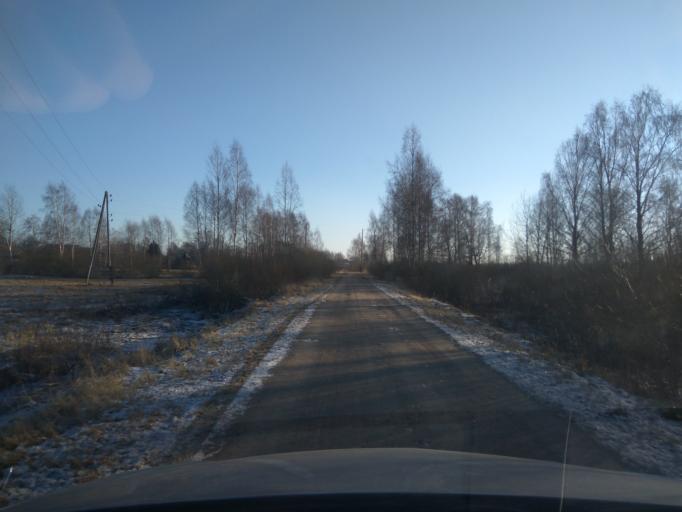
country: LV
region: Kuldigas Rajons
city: Kuldiga
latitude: 56.9603
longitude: 21.9641
